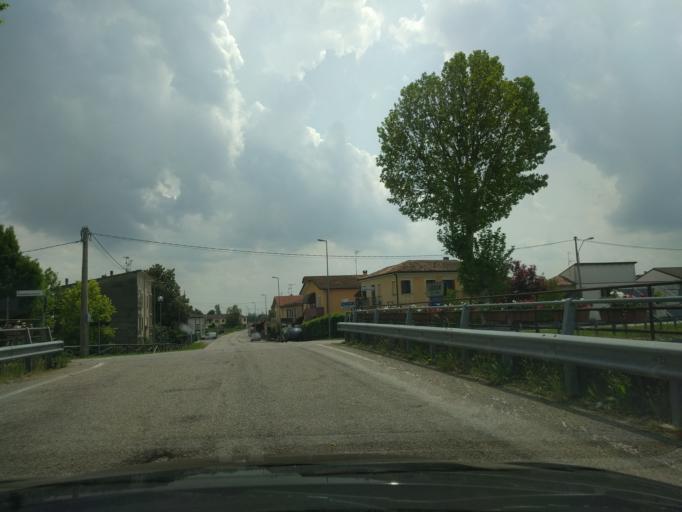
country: IT
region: Veneto
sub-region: Provincia di Rovigo
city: Lendinara
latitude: 45.0790
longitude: 11.5586
